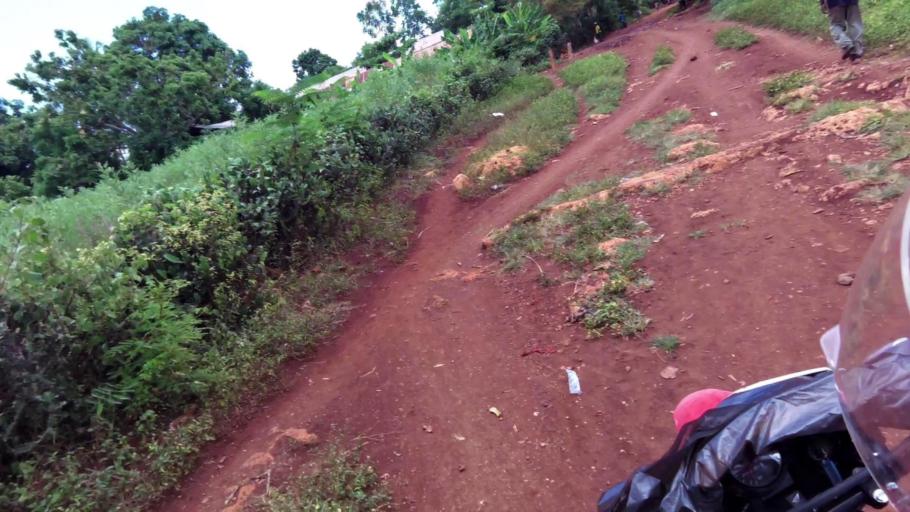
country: HT
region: Ouest
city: Anse a Galets
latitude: 18.7795
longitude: -72.8629
